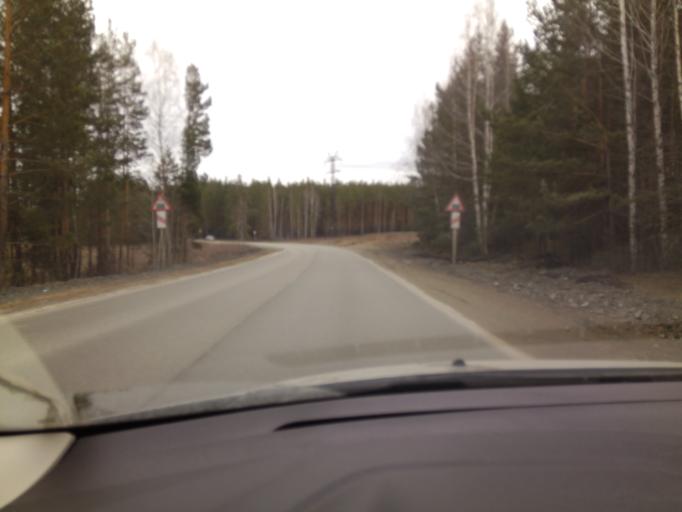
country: RU
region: Chelyabinsk
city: Kyshtym
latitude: 55.7079
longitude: 60.5802
